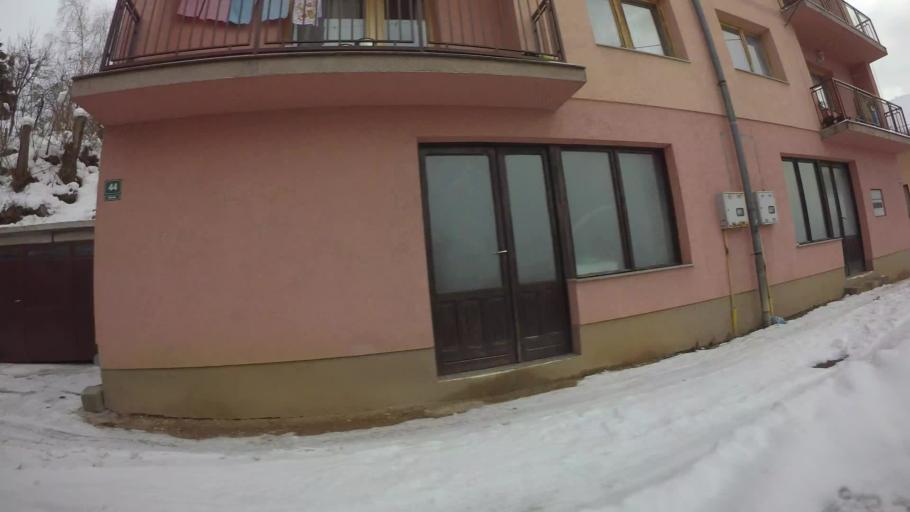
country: BA
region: Federation of Bosnia and Herzegovina
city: Kobilja Glava
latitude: 43.8707
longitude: 18.4388
